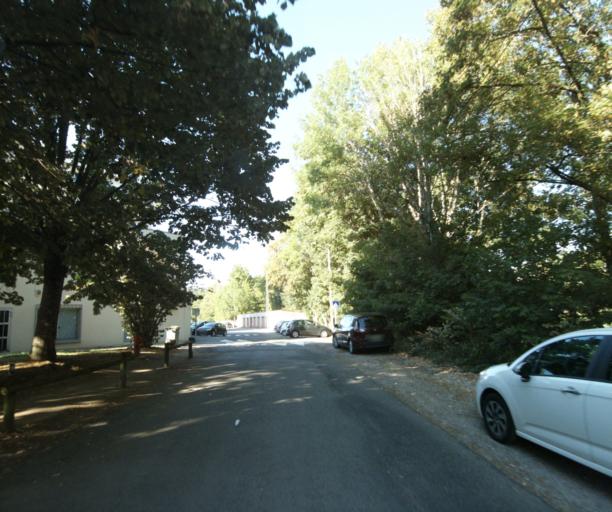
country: FR
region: Lorraine
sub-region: Departement des Vosges
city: Chantraine
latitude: 48.1587
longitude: 6.4539
